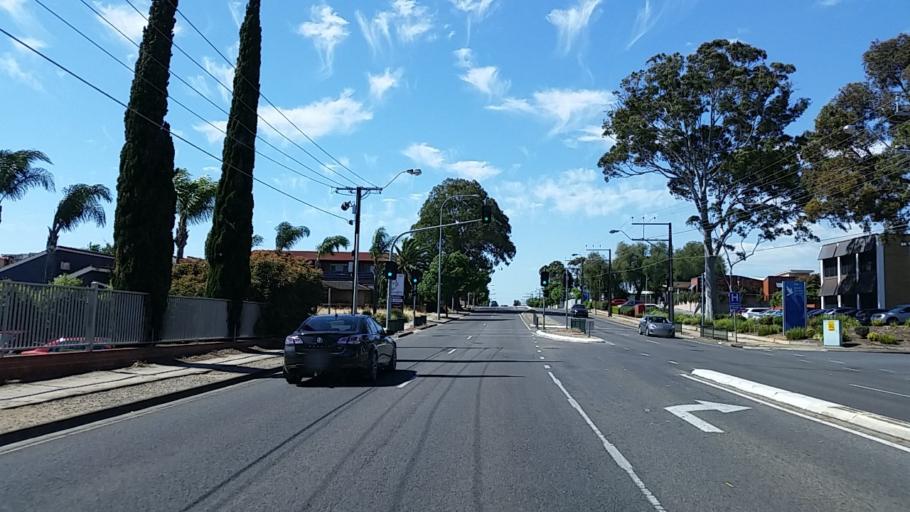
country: AU
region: South Australia
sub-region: Campbelltown
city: Campbelltown
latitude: -34.8830
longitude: 138.6605
